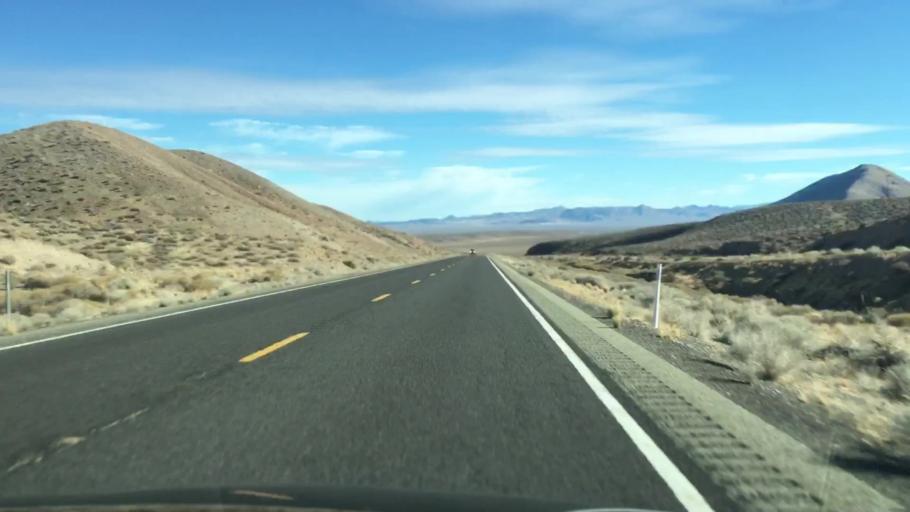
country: US
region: Nevada
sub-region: Lyon County
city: Yerington
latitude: 39.0383
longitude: -118.9337
